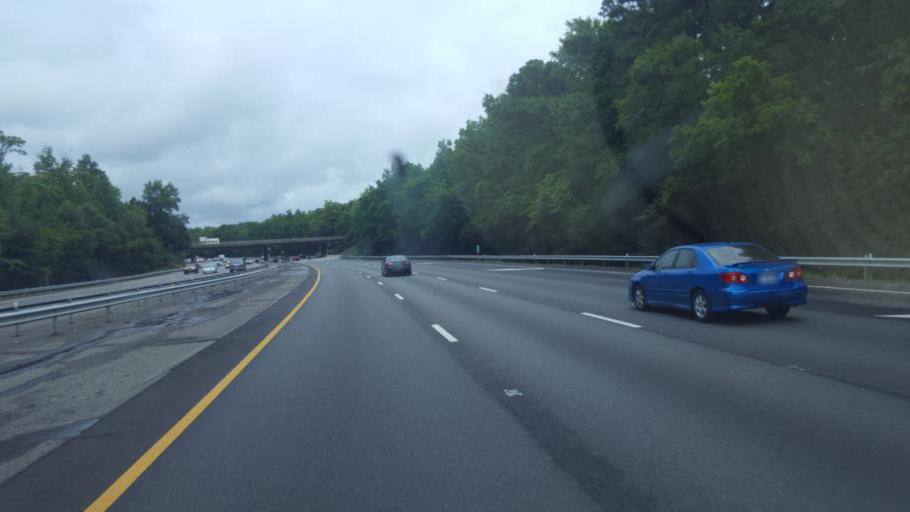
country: US
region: Virginia
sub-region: Henrico County
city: Chamberlayne
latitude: 37.6161
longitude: -77.4441
